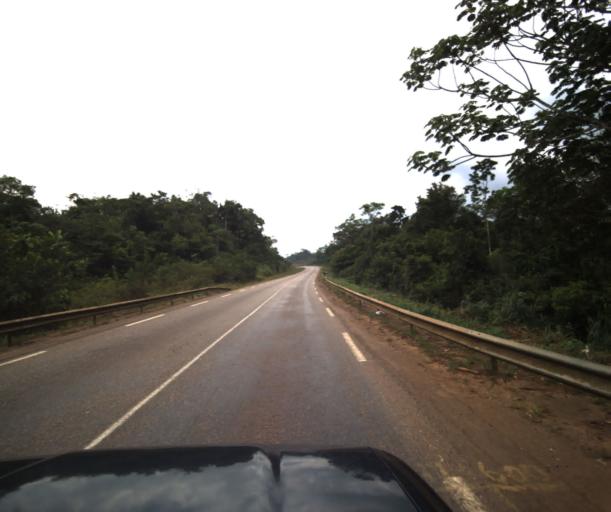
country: CM
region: Littoral
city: Edea
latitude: 3.8599
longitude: 10.0795
